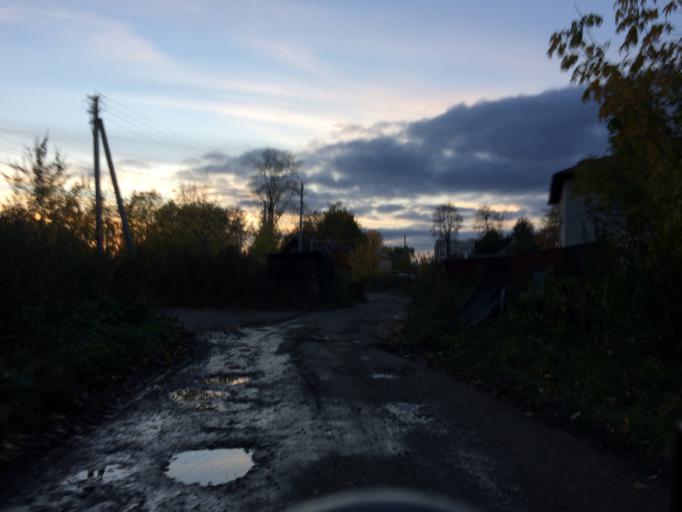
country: RU
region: Mariy-El
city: Yoshkar-Ola
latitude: 56.6404
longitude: 47.9118
